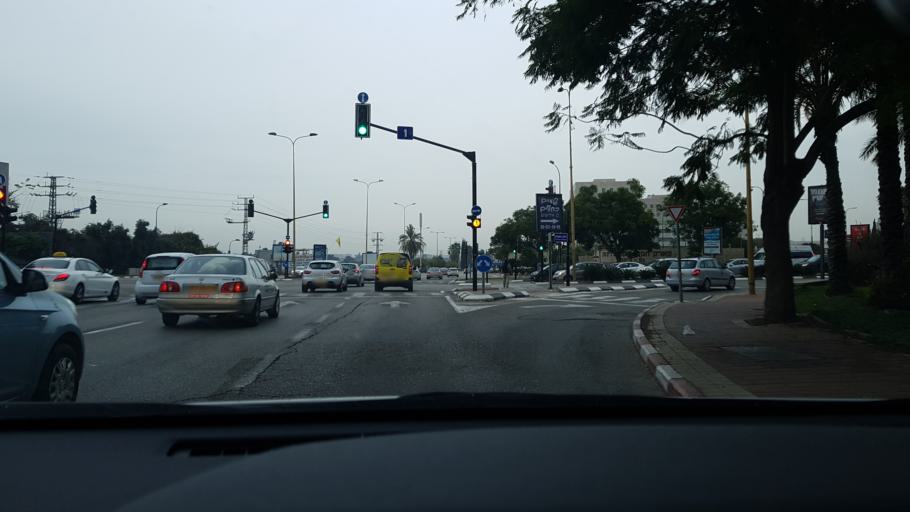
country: IL
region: Central District
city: Ness Ziona
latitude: 31.9113
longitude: 34.8034
